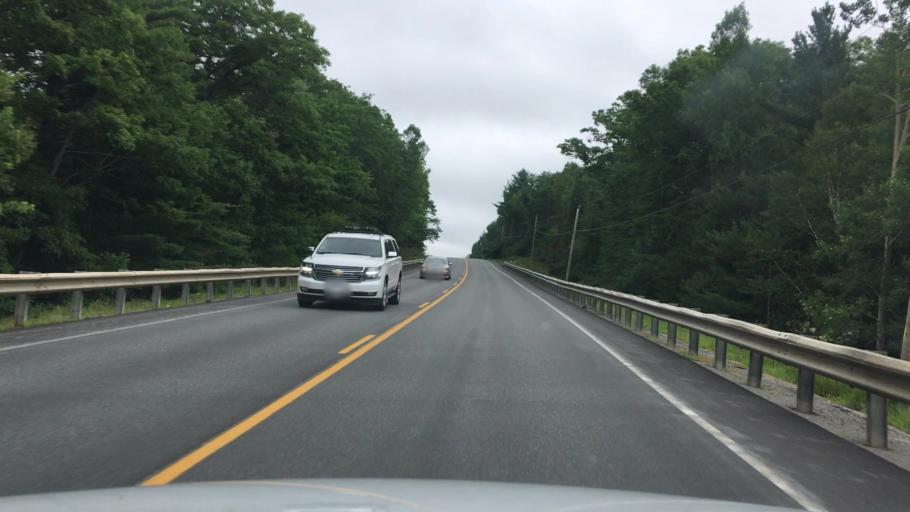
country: US
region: Maine
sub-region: Hancock County
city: Franklin
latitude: 44.8386
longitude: -68.1642
